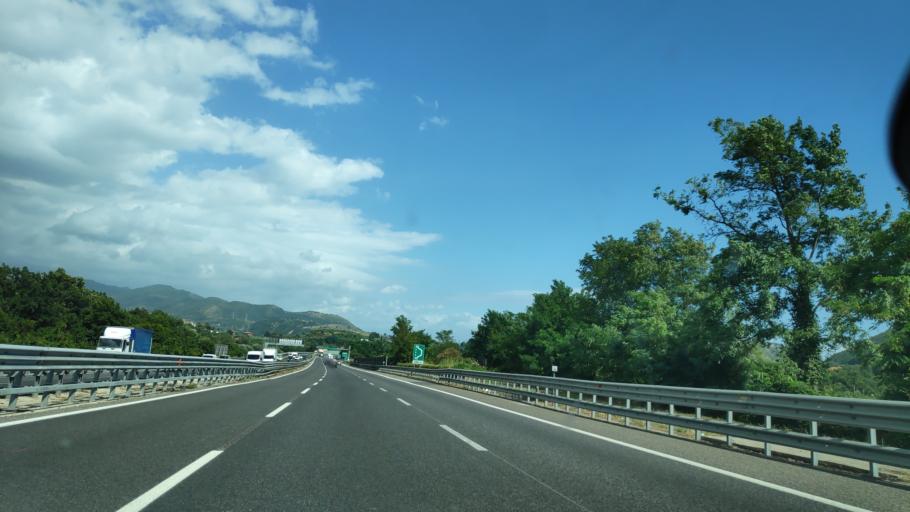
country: IT
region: Campania
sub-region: Provincia di Salerno
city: San Mango Piemonte
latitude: 40.6877
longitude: 14.8437
